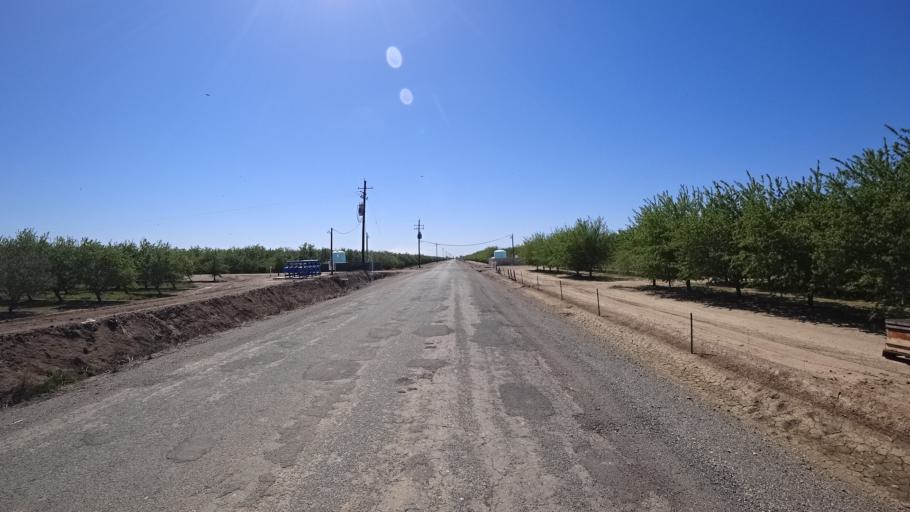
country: US
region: California
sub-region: Glenn County
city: Orland
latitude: 39.6467
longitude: -122.2346
